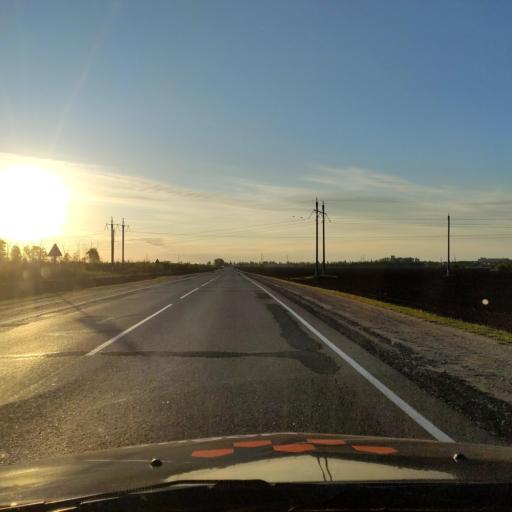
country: RU
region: Orjol
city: Livny
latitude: 52.4405
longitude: 37.5539
